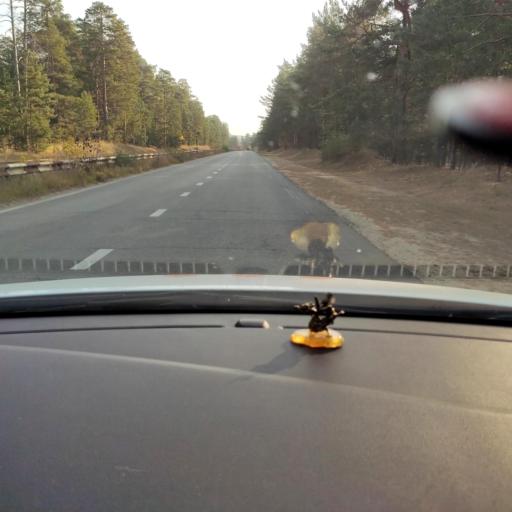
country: RU
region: Tatarstan
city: Osinovo
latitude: 55.8256
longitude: 48.9035
